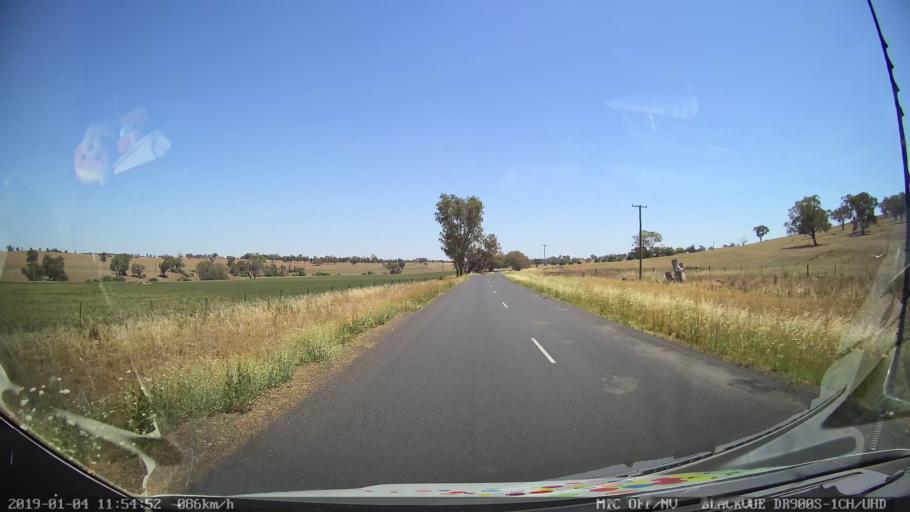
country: AU
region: New South Wales
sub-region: Cabonne
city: Molong
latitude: -32.8608
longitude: 148.7270
